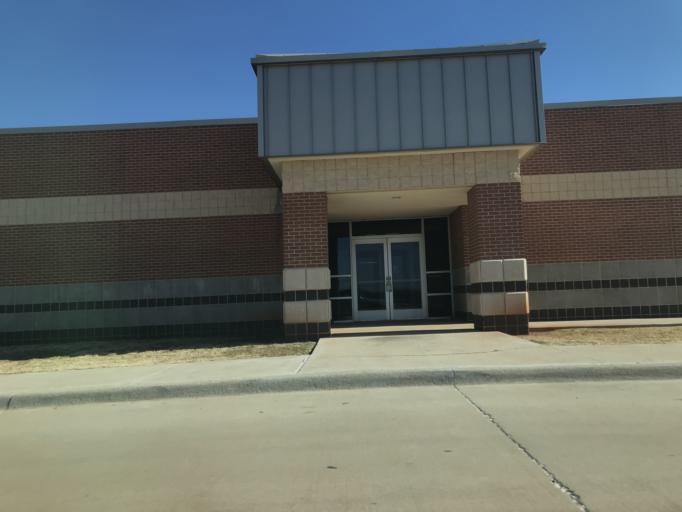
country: US
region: Texas
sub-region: Taylor County
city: Abilene
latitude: 32.4418
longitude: -99.7083
